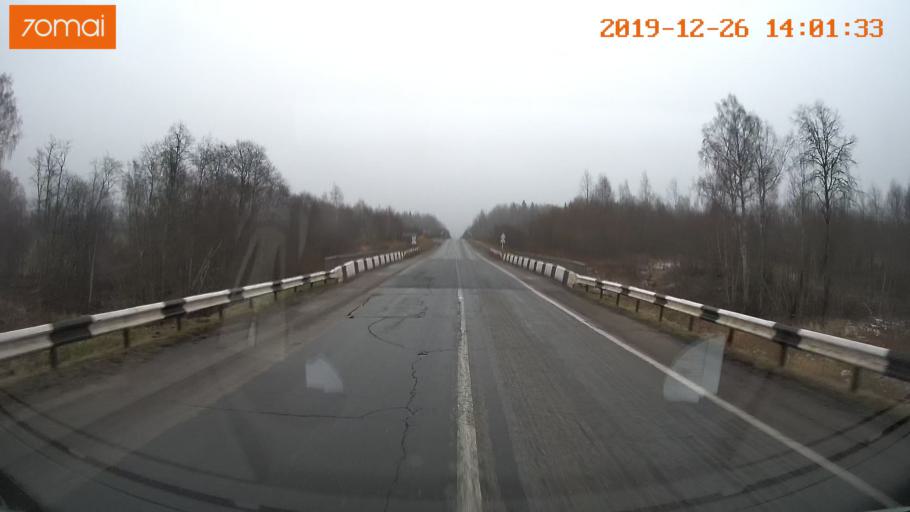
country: RU
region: Jaroslavl
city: Poshekhon'ye
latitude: 58.5496
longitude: 38.7661
